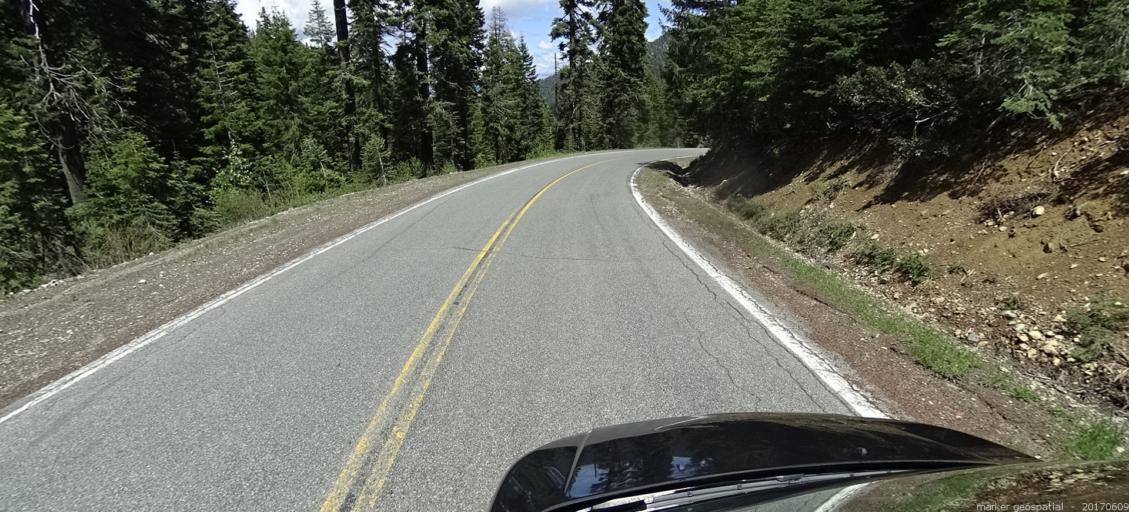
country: US
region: California
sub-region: Siskiyou County
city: Yreka
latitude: 41.4008
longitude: -122.9892
